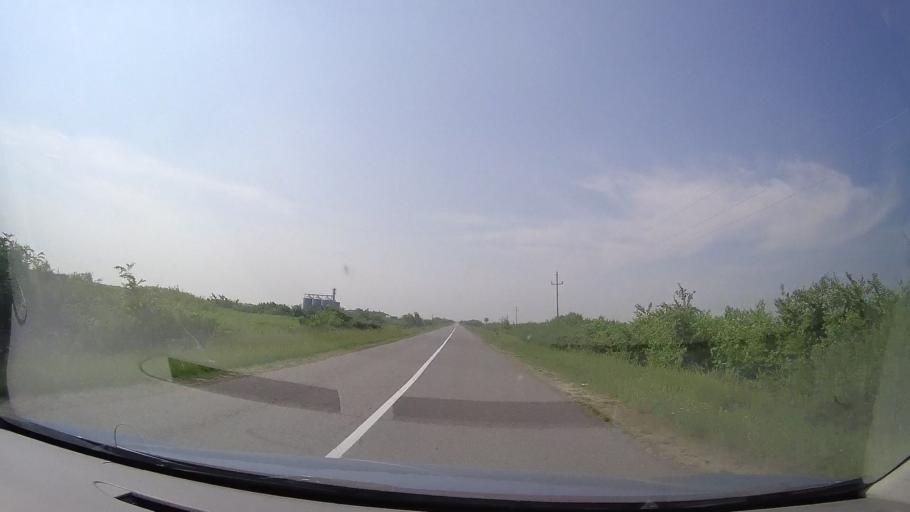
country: RS
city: Jarkovac
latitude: 45.2577
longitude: 20.7637
